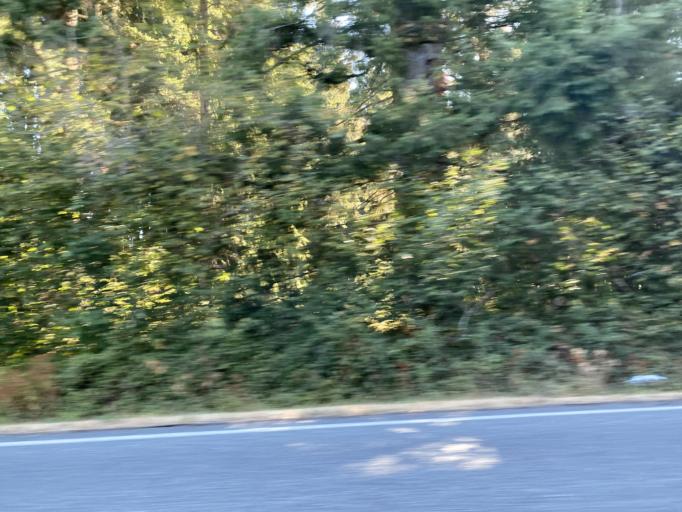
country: US
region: Washington
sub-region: Thurston County
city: Tanglewilde-Thompson Place
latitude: 46.9956
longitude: -122.7386
